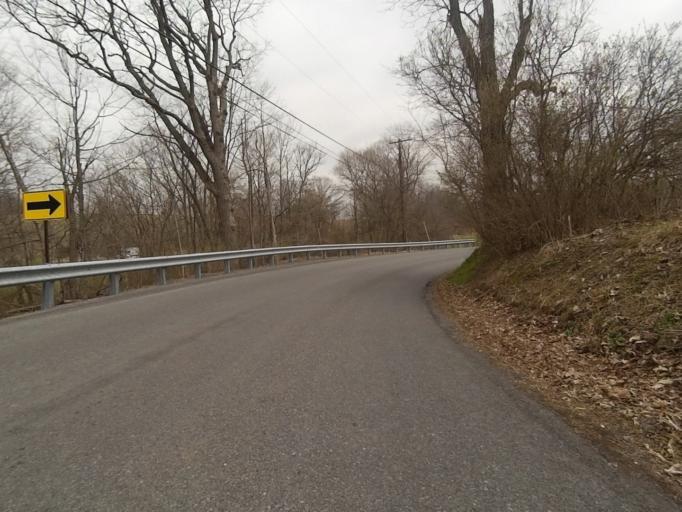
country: US
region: Pennsylvania
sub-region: Centre County
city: Boalsburg
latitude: 40.7923
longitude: -77.7821
